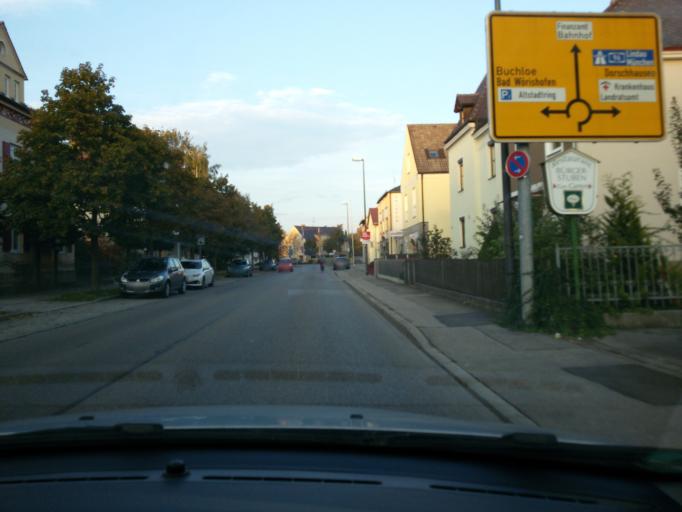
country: DE
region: Bavaria
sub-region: Swabia
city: Mindelheim
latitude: 48.0456
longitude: 10.4900
